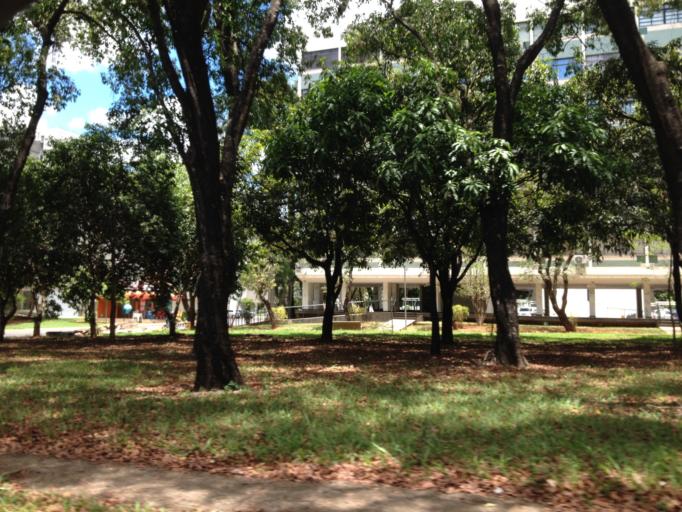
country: BR
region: Federal District
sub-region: Brasilia
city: Brasilia
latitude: -15.8175
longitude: -47.9074
